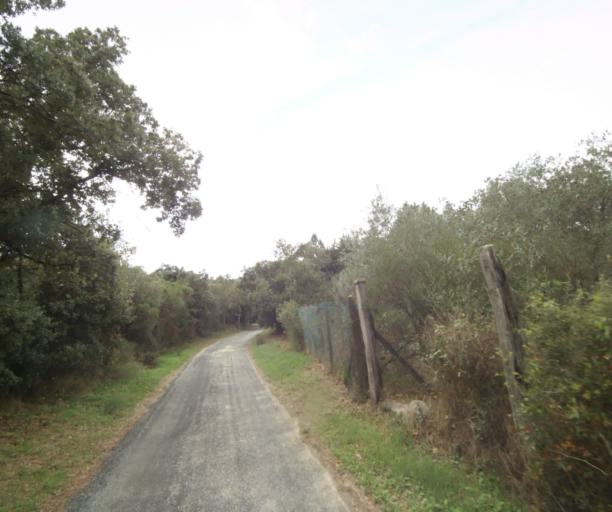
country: FR
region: Languedoc-Roussillon
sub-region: Departement des Pyrenees-Orientales
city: Argelers
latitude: 42.5369
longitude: 3.0006
